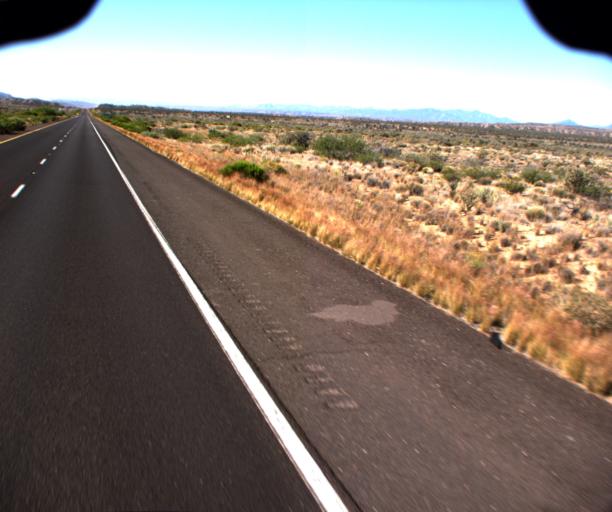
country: US
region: Arizona
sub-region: Mohave County
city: Kingman
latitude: 35.1078
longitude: -113.6667
